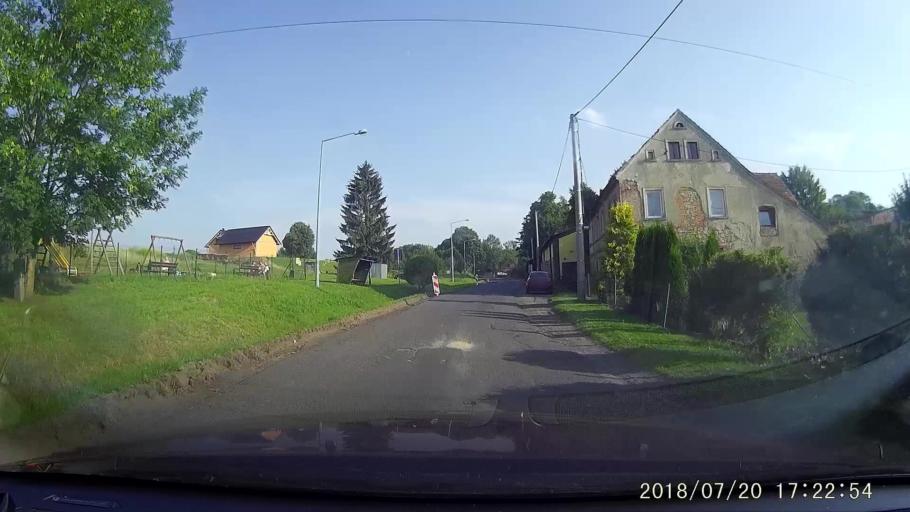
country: PL
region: Lower Silesian Voivodeship
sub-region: Powiat lubanski
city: Lesna
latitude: 50.9760
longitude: 15.2890
